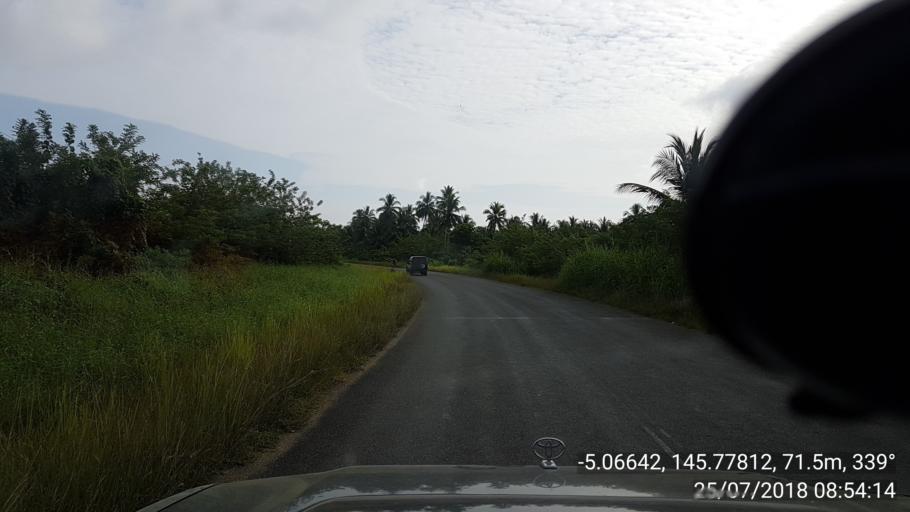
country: PG
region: Madang
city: Madang
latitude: -5.0665
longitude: 145.7782
